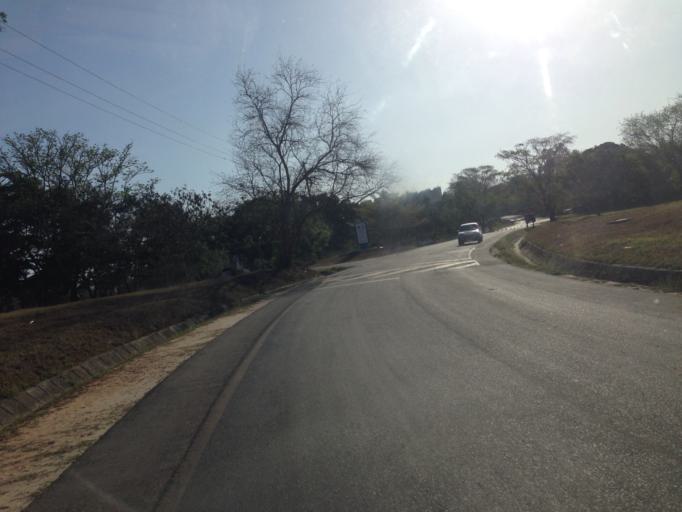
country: TZ
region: Dar es Salaam
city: Magomeni
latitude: -6.7732
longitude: 39.2129
